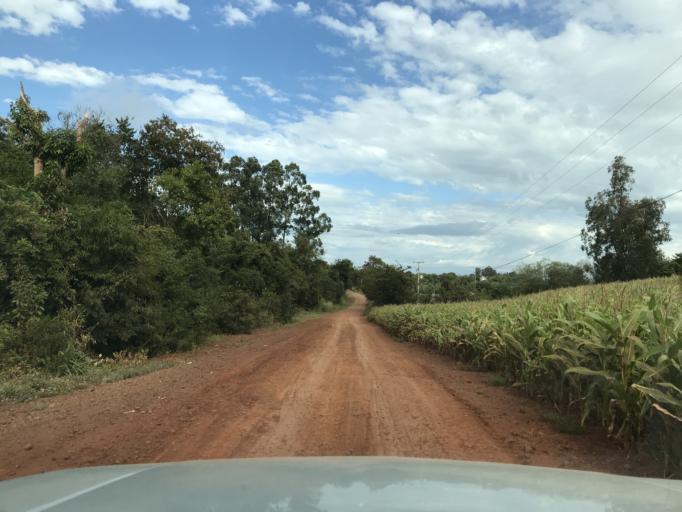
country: BR
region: Parana
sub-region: Palotina
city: Palotina
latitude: -24.3212
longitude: -53.8063
